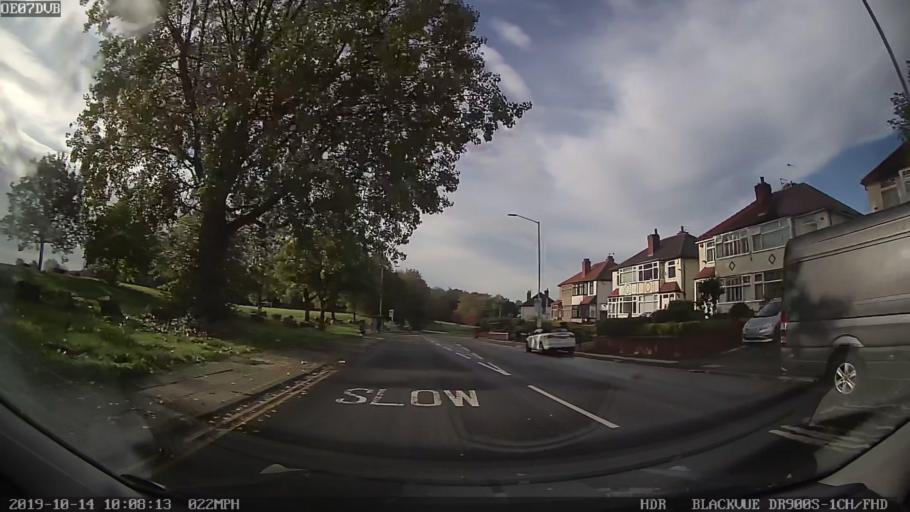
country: GB
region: England
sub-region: Manchester
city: Failsworth
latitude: 53.5187
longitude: -2.1852
